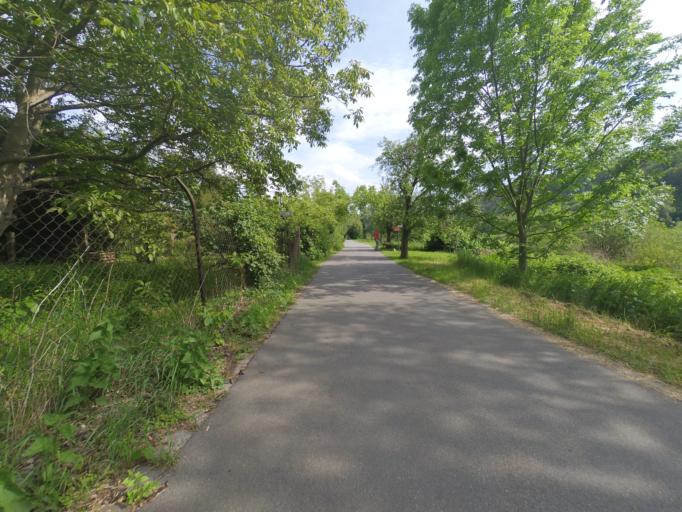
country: DE
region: Saxony
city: Meissen
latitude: 51.1484
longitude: 13.4935
